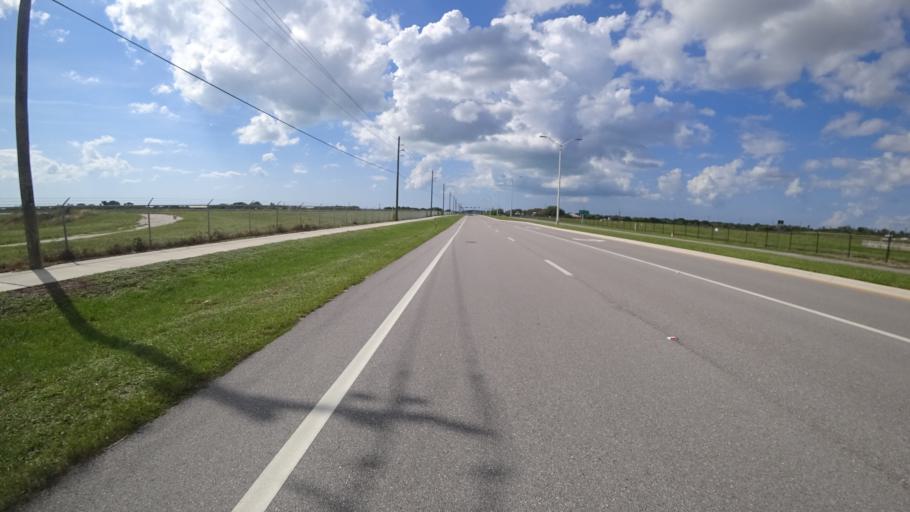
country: US
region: Florida
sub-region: Manatee County
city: Bayshore Gardens
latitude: 27.4478
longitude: -82.6251
